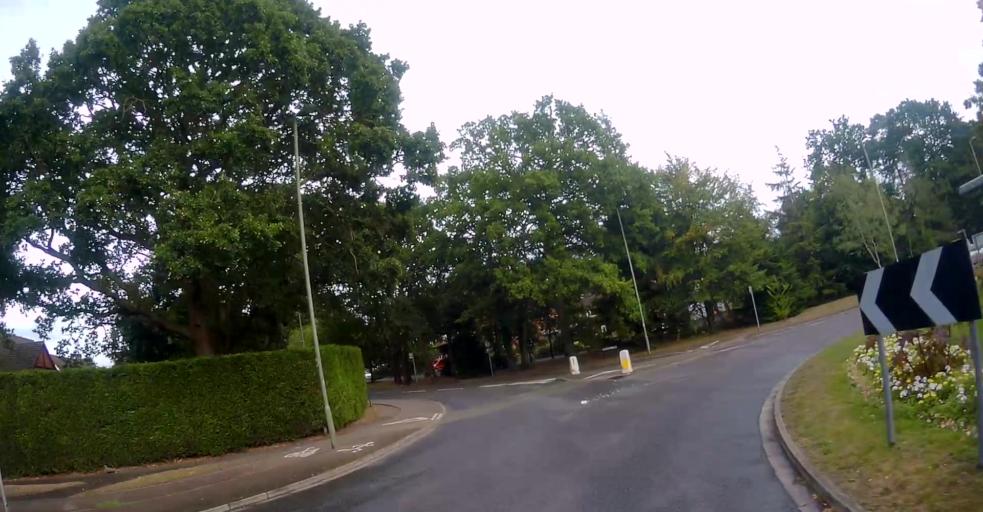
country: GB
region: England
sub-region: Surrey
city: Knaphill
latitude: 51.3117
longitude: -0.6139
